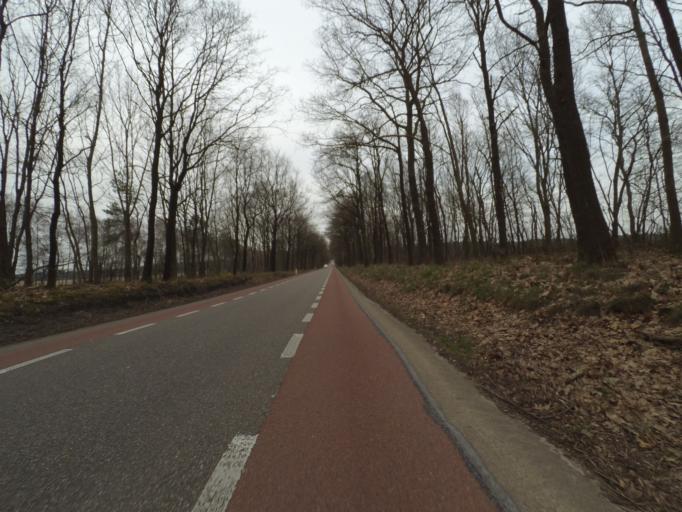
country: NL
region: Gelderland
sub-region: Gemeente Arnhem
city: Hoogkamp
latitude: 52.0975
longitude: 5.8789
